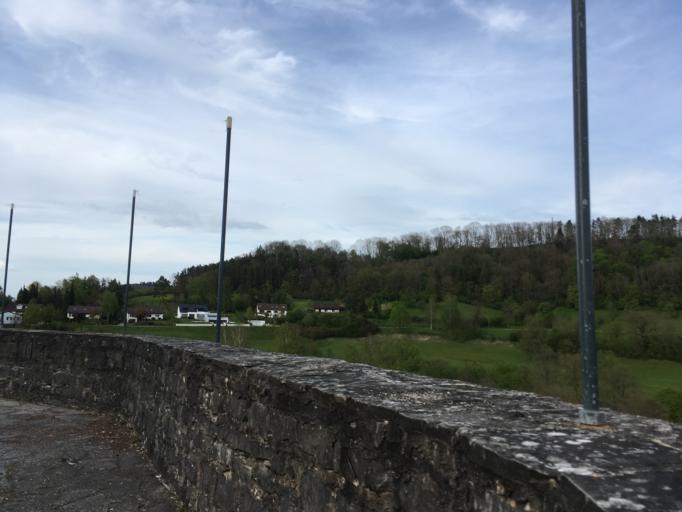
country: DE
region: Baden-Wuerttemberg
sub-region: Regierungsbezirk Stuttgart
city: Vellberg
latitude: 49.0879
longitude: 9.8833
